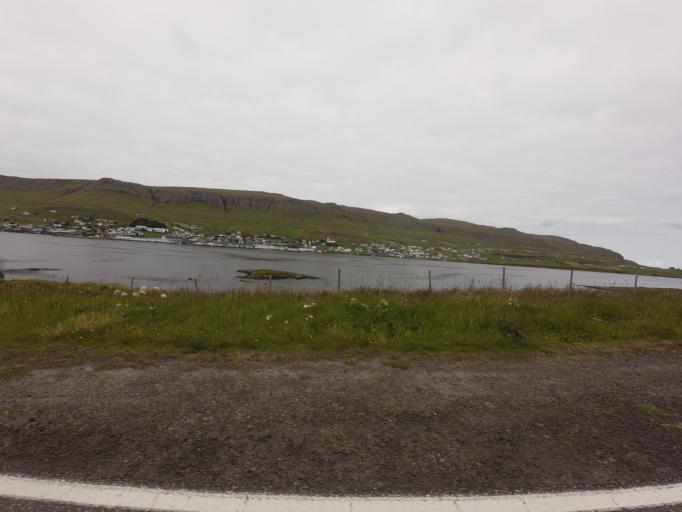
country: FO
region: Suduroy
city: Tvoroyri
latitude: 61.5463
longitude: -6.8155
